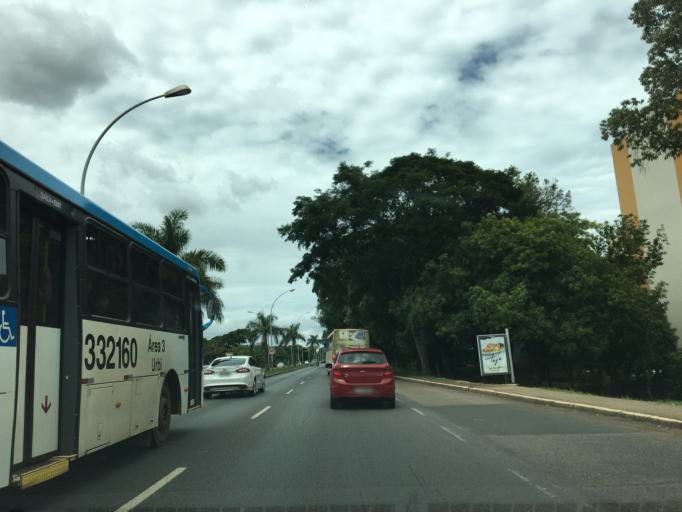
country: BR
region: Federal District
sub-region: Brasilia
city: Brasilia
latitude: -15.8197
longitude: -47.9032
